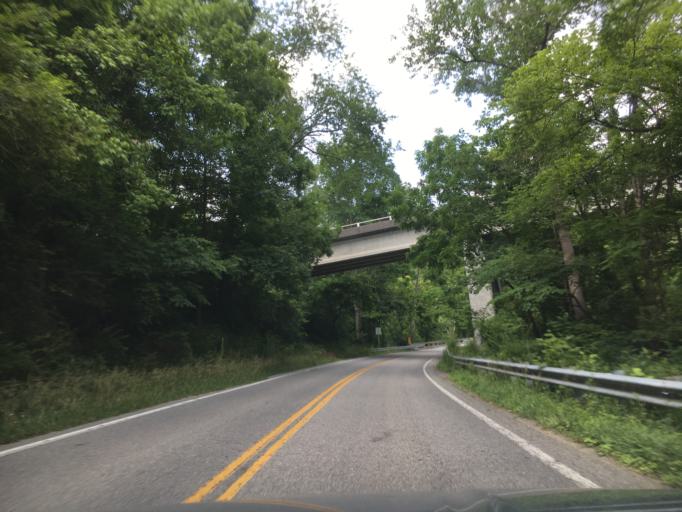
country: US
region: Virginia
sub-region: Roanoke County
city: Cave Spring
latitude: 37.1927
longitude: -80.0010
